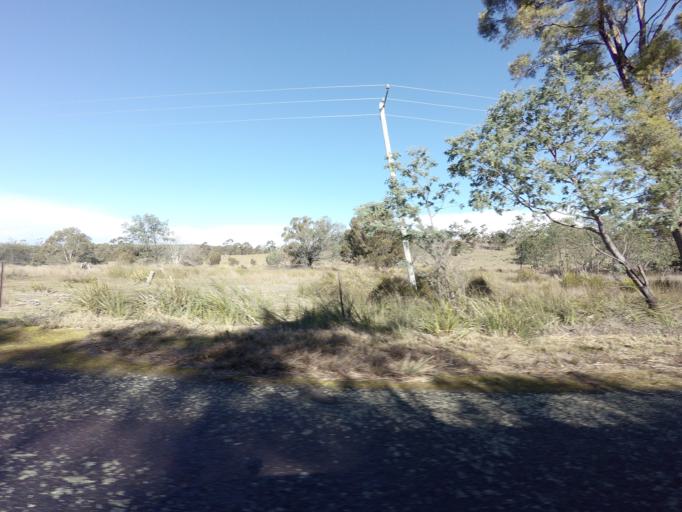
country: AU
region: Tasmania
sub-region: Sorell
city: Sorell
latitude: -42.3621
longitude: 147.9516
